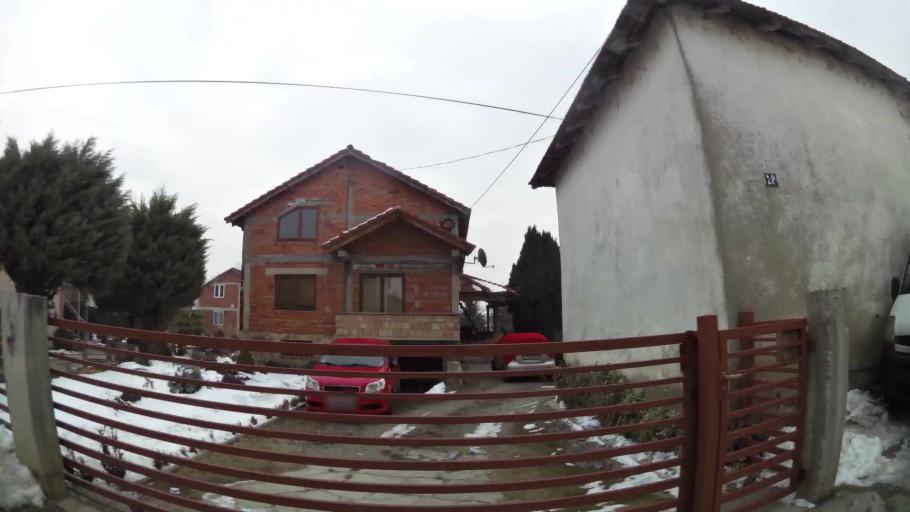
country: MK
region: Saraj
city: Saraj
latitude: 42.0477
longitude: 21.3588
